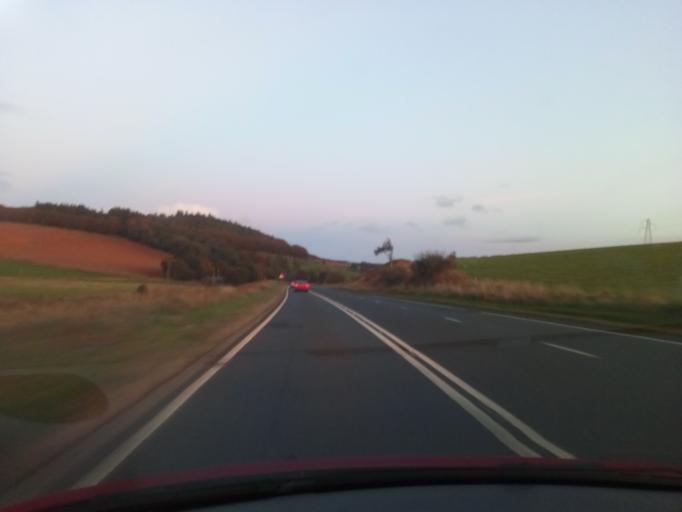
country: GB
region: Scotland
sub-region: The Scottish Borders
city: Lauder
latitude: 55.7838
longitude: -2.8150
